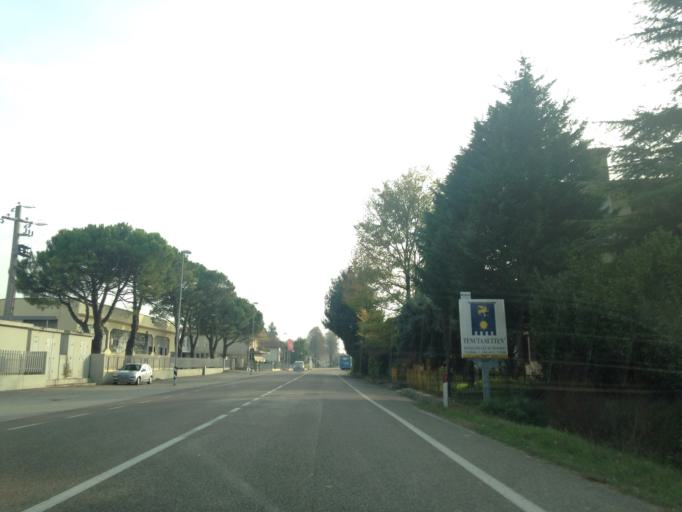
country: IT
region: Veneto
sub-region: Provincia di Treviso
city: Mansue
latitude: 45.8274
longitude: 12.5377
